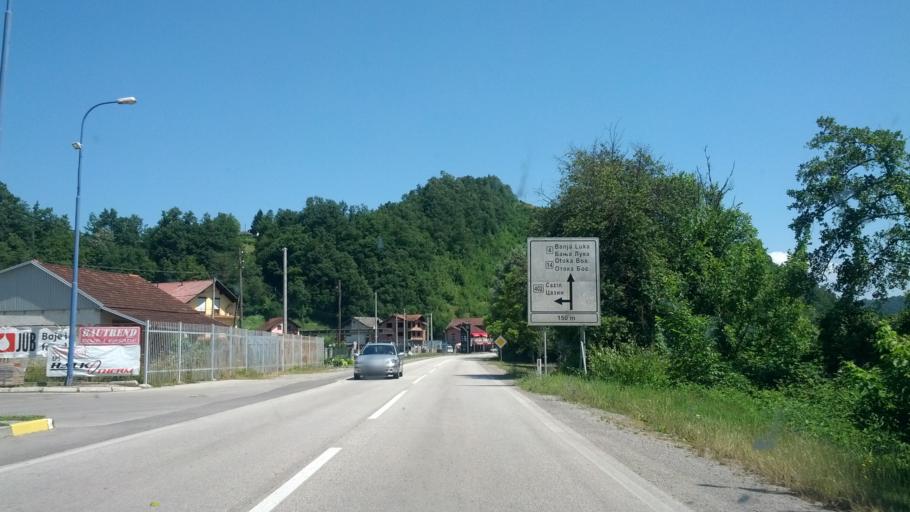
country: BA
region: Federation of Bosnia and Herzegovina
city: Otoka
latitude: 44.9385
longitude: 16.1611
